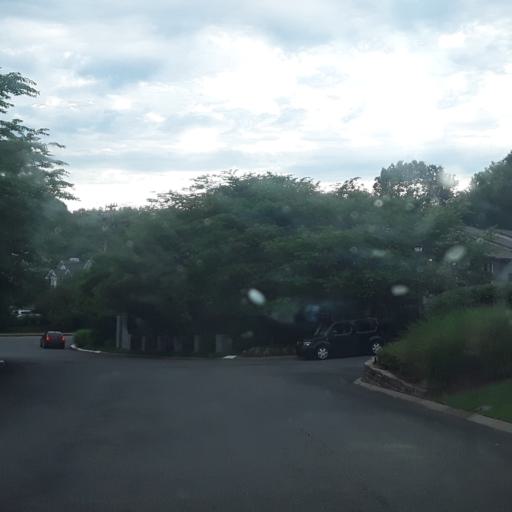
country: US
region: Tennessee
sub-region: Wilson County
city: Green Hill
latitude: 36.1659
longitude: -86.5974
